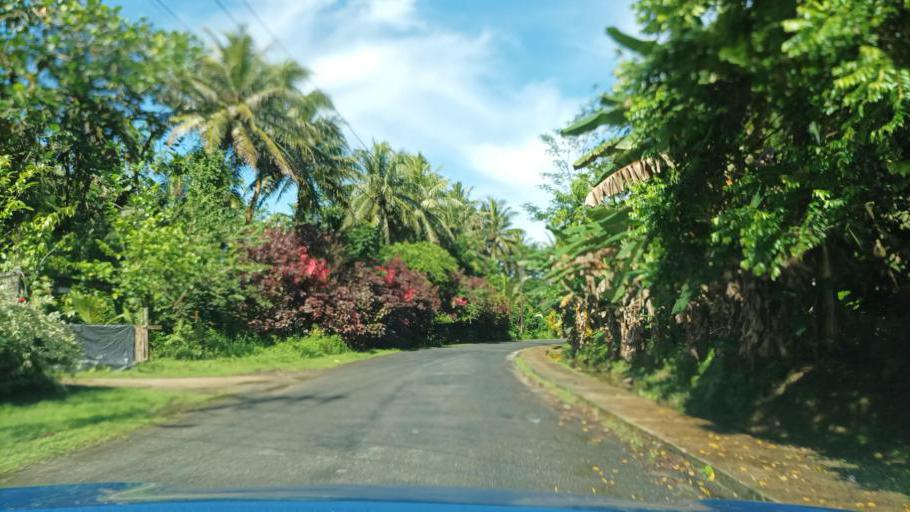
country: FM
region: Pohnpei
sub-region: Sokehs Municipality
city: Palikir - National Government Center
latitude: 6.9241
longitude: 158.1660
